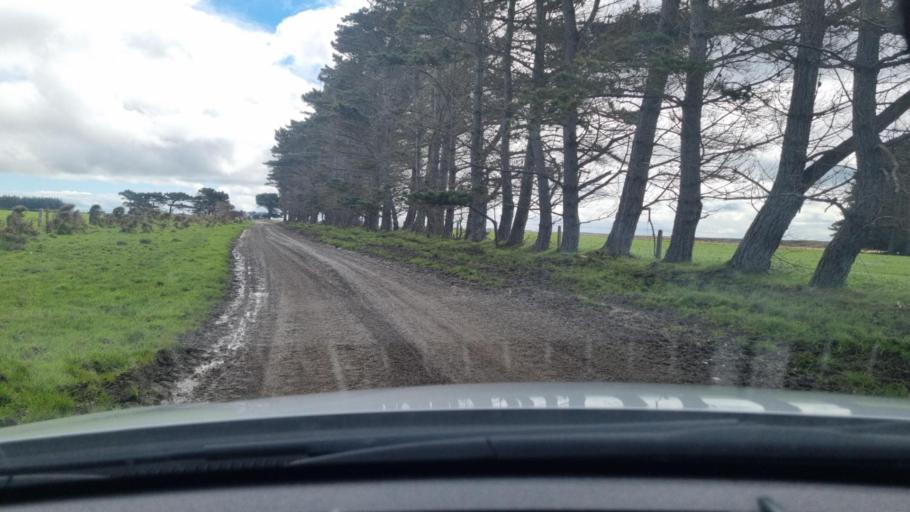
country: NZ
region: Southland
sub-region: Invercargill City
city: Bluff
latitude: -46.5668
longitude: 168.5021
